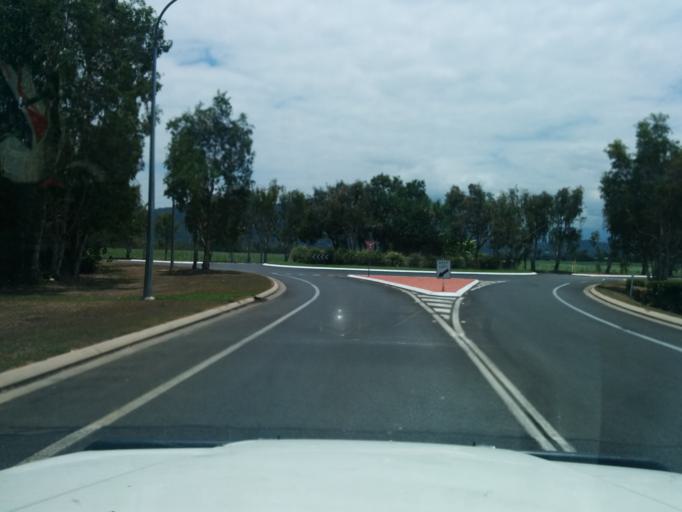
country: AU
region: Queensland
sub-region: Cairns
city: Redlynch
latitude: -16.8503
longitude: 145.7334
